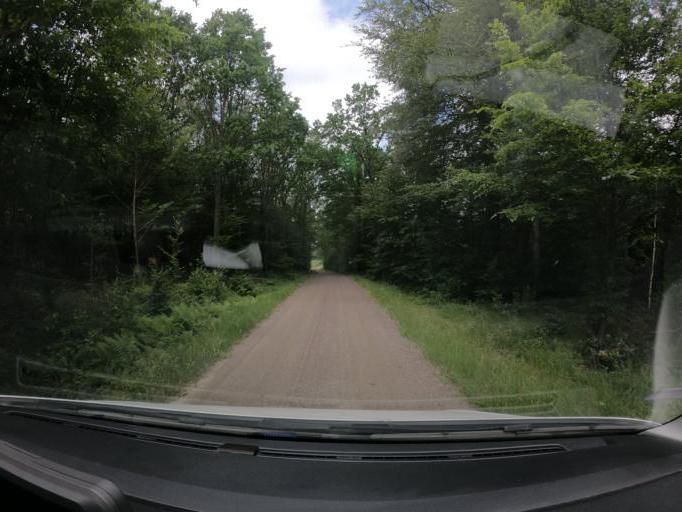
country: SE
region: Skane
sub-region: Hassleholms Kommun
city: Sosdala
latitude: 56.0566
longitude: 13.5689
